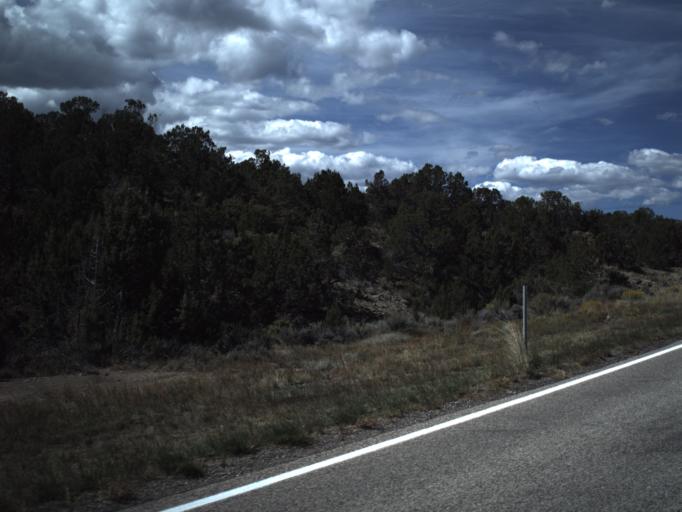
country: US
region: Utah
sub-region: Washington County
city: Enterprise
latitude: 37.4535
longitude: -113.6222
